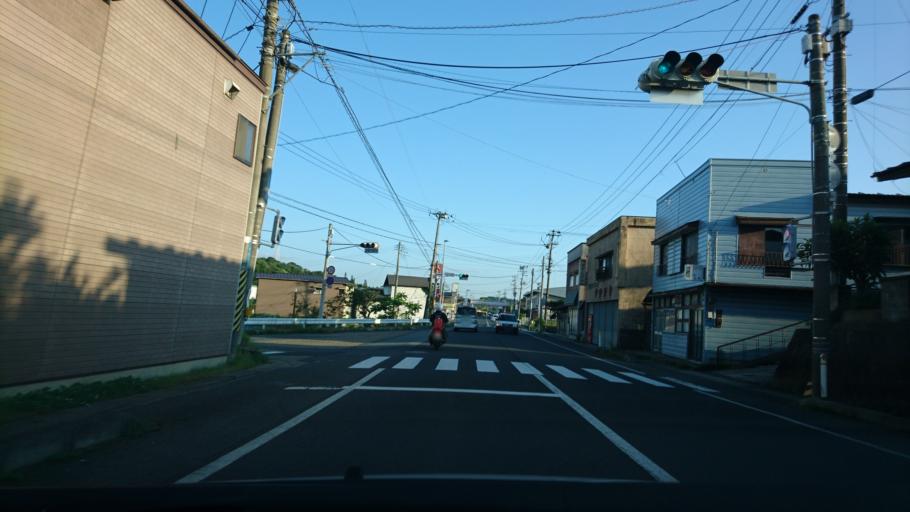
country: JP
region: Iwate
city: Ichinoseki
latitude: 38.9178
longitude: 141.1320
